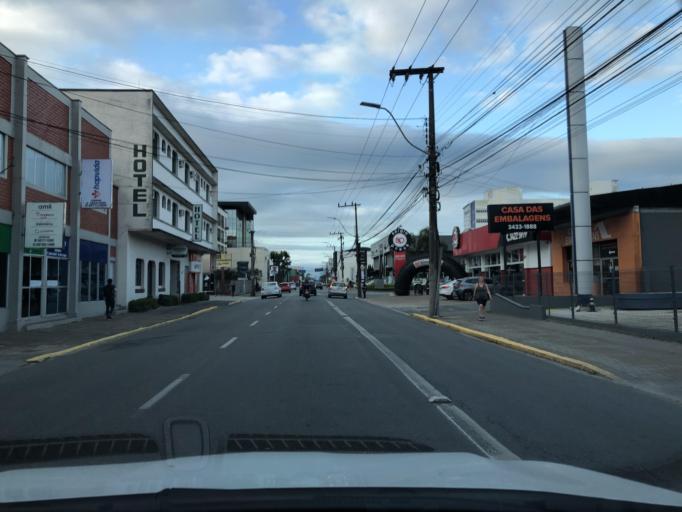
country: BR
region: Santa Catarina
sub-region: Joinville
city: Joinville
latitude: -26.2895
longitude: -48.8486
